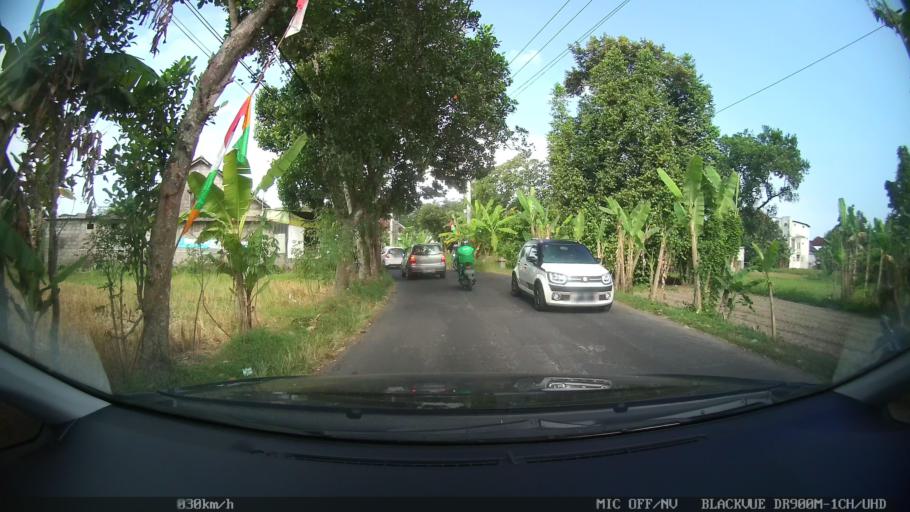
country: ID
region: Daerah Istimewa Yogyakarta
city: Depok
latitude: -7.7292
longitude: 110.4129
